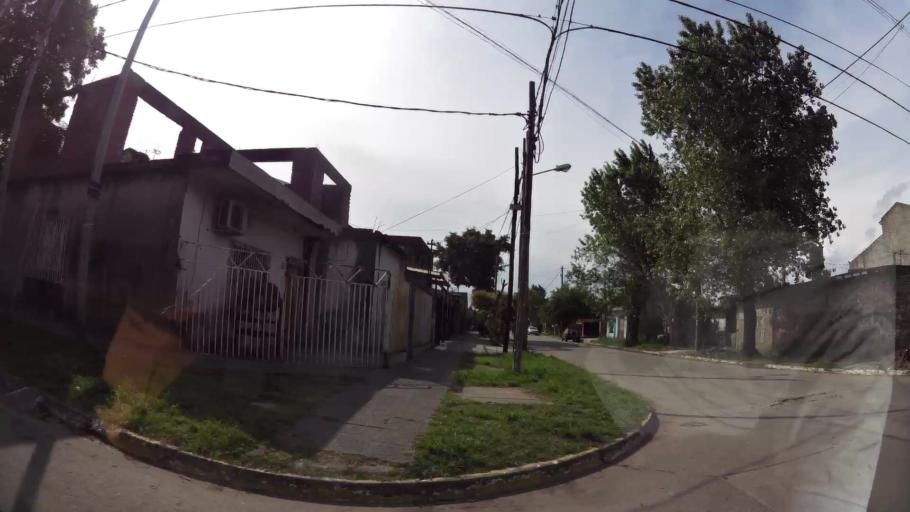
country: AR
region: Buenos Aires
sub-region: Partido de Quilmes
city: Quilmes
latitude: -34.7705
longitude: -58.2519
